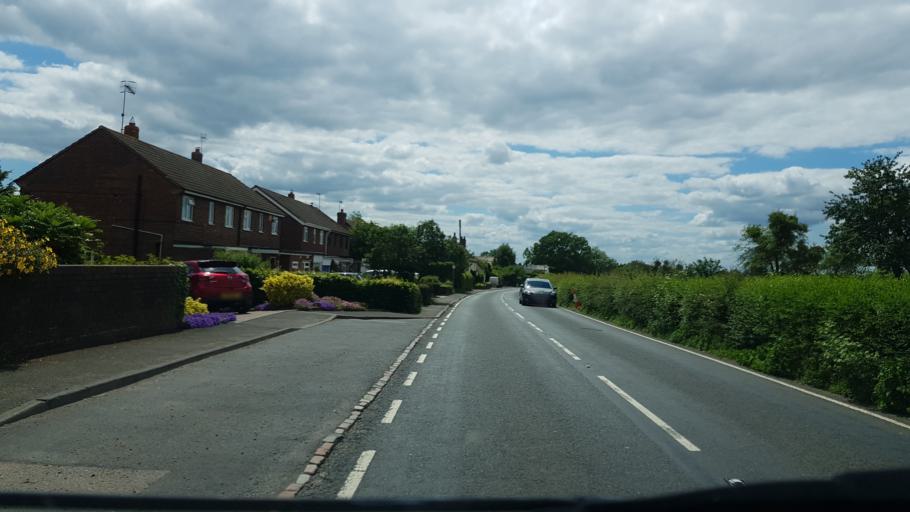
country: GB
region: England
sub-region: Worcestershire
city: Bromsgrove
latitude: 52.2642
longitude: -2.0539
